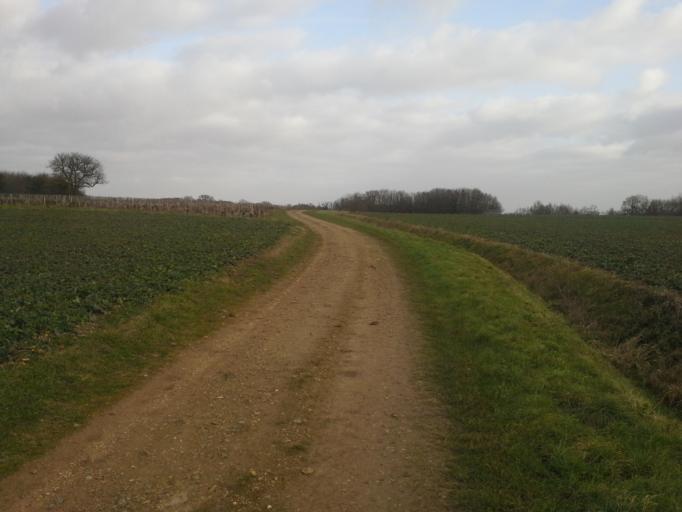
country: FR
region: Centre
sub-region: Departement du Loir-et-Cher
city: Villiers-sur-Loir
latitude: 47.8144
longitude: 0.9757
